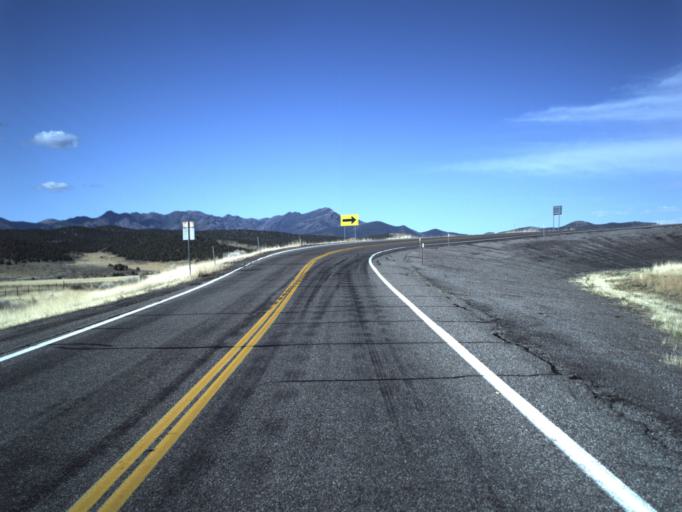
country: US
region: Utah
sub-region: Millard County
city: Fillmore
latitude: 39.1439
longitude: -112.2386
